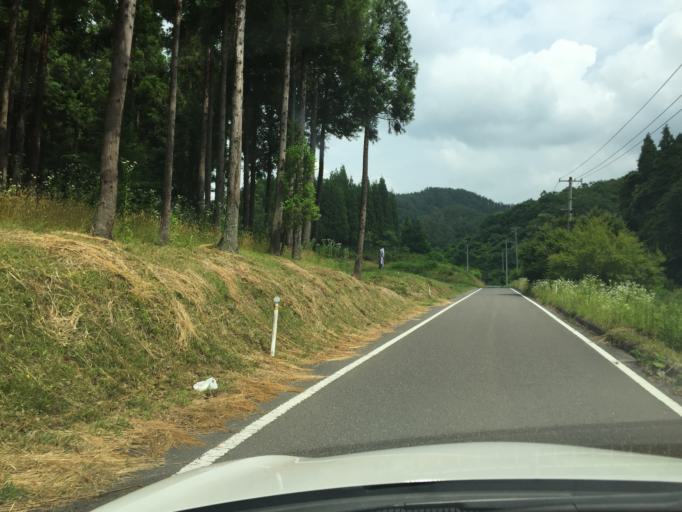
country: JP
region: Fukushima
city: Sukagawa
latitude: 37.2976
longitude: 140.5021
